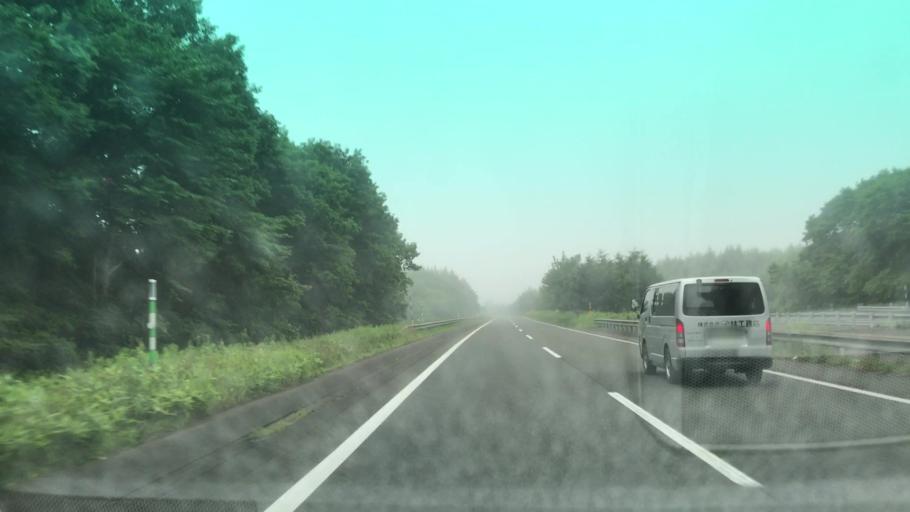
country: JP
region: Hokkaido
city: Chitose
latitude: 42.7912
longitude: 141.6269
